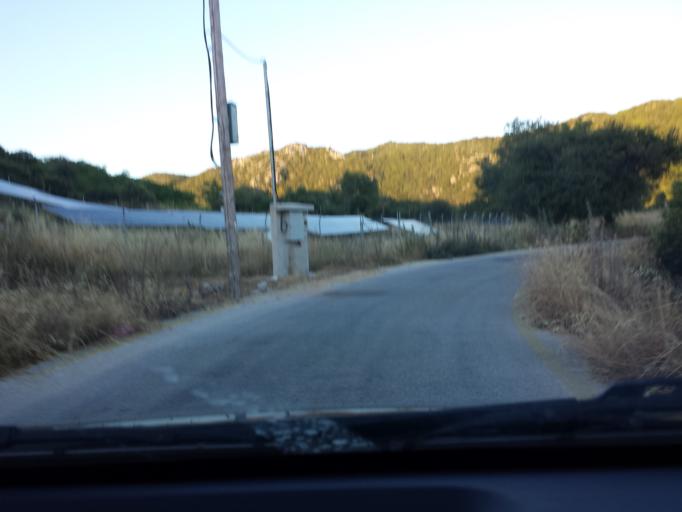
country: GR
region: Ionian Islands
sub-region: Nomos Kerkyras
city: Acharavi
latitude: 39.7405
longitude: 19.8372
